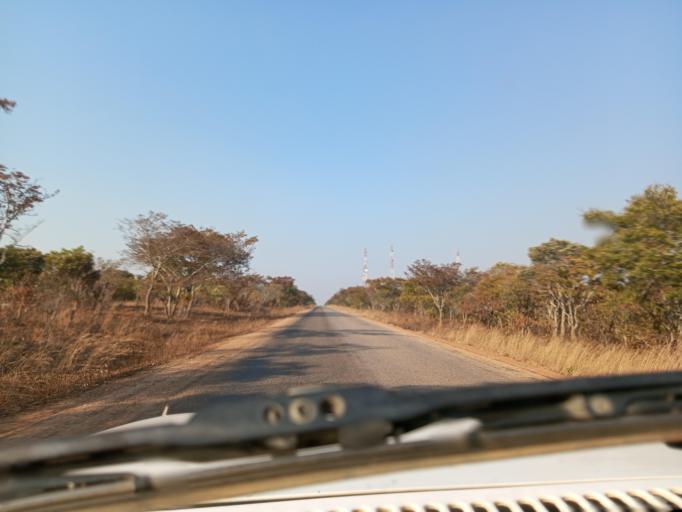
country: ZM
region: Northern
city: Mpika
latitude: -12.4134
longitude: 31.0829
